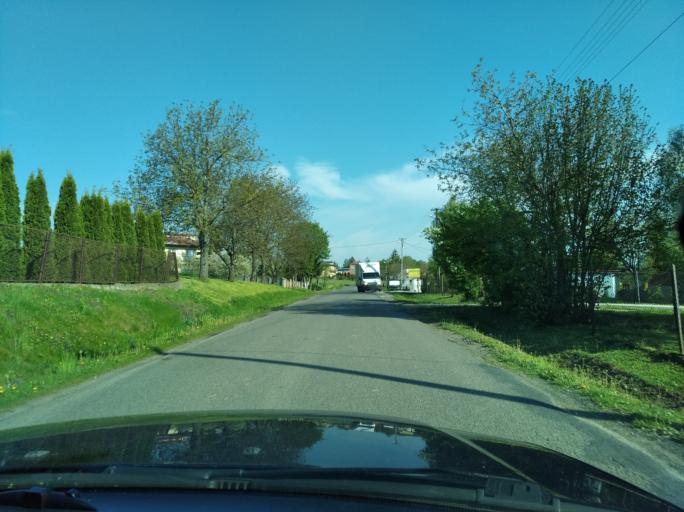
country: PL
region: Subcarpathian Voivodeship
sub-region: Powiat jaroslawski
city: Pruchnik
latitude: 49.8952
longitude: 22.5544
